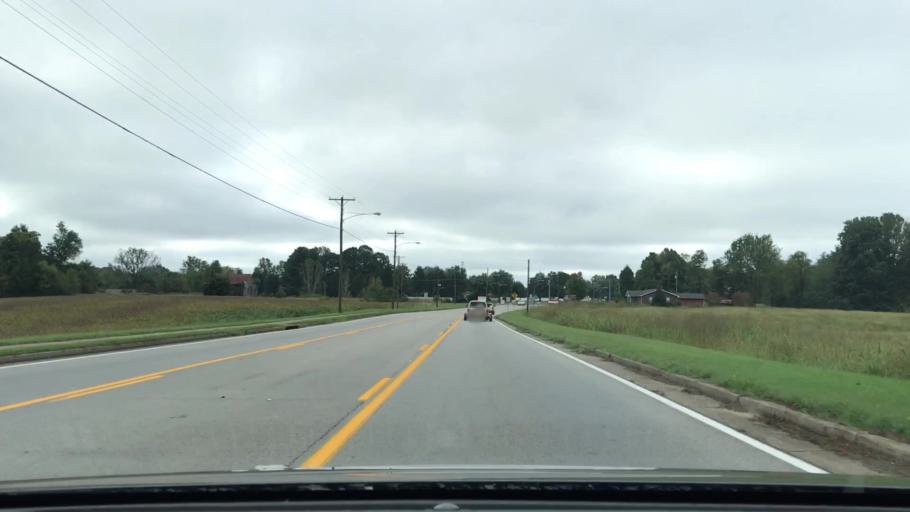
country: US
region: Kentucky
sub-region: Russell County
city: Jamestown
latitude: 37.0014
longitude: -85.0731
